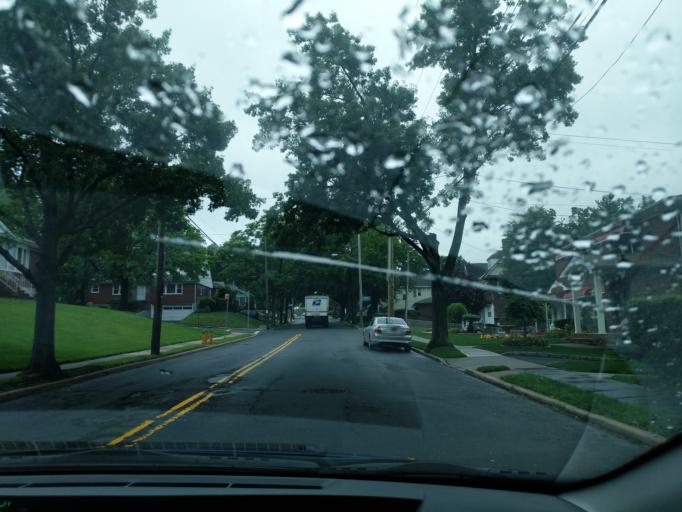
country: US
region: New Jersey
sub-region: Hudson County
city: Bayonne
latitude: 40.6235
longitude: -74.1247
